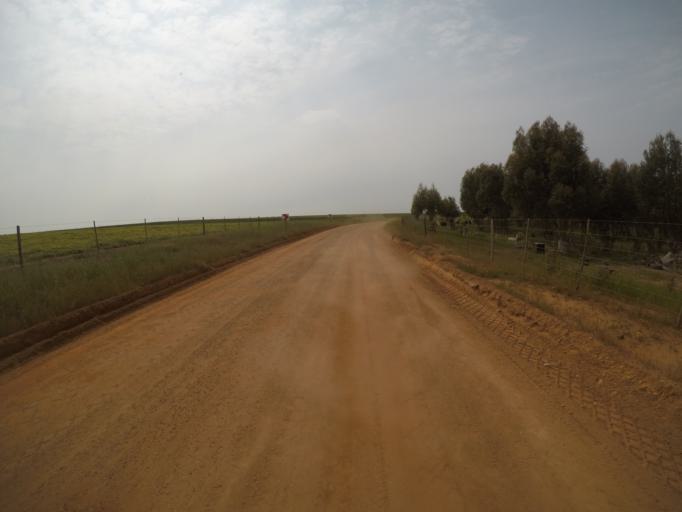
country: ZA
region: Western Cape
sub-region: City of Cape Town
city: Kraaifontein
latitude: -33.7238
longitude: 18.6557
